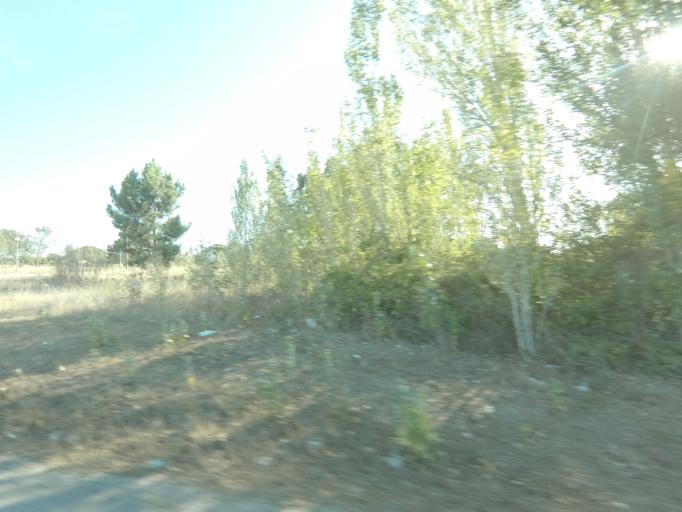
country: PT
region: Setubal
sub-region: Palmela
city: Pinhal Novo
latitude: 38.6144
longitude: -8.9514
